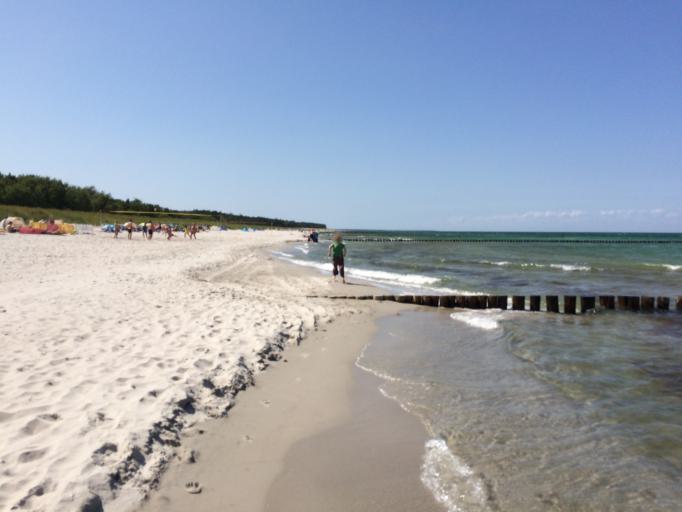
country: DE
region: Mecklenburg-Vorpommern
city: Zingst
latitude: 54.4436
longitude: 12.6531
